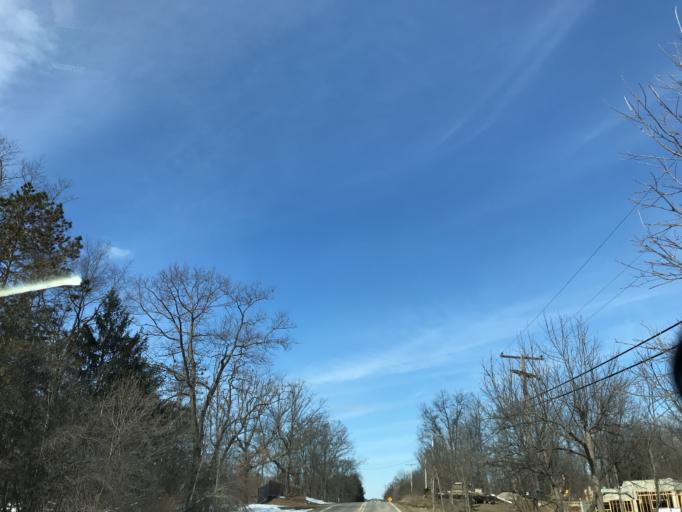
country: US
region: Michigan
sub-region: Livingston County
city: Whitmore Lake
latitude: 42.4185
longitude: -83.7428
